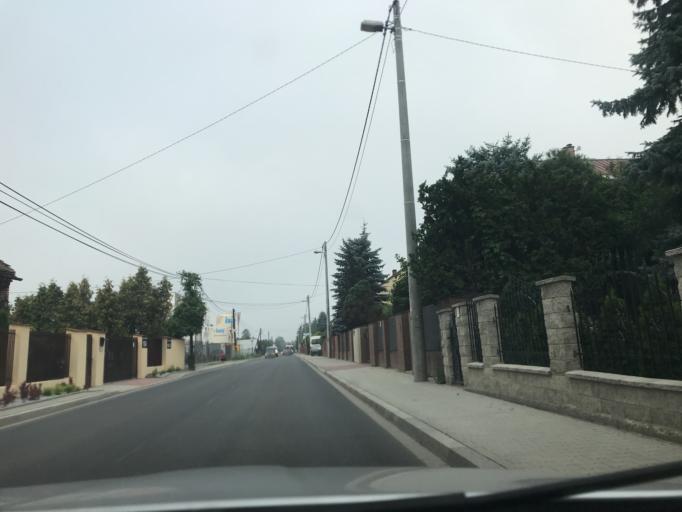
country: PL
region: Lesser Poland Voivodeship
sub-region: Powiat krakowski
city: Ochojno
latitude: 50.0074
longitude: 19.9742
